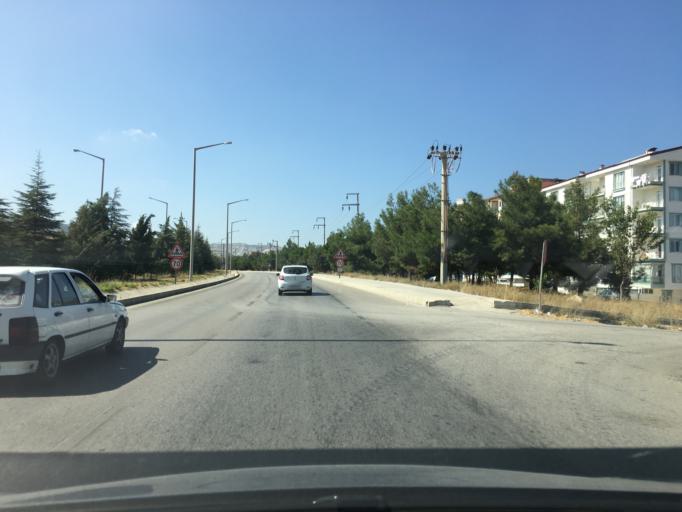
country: TR
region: Burdur
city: Burdur
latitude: 37.7277
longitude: 30.3019
